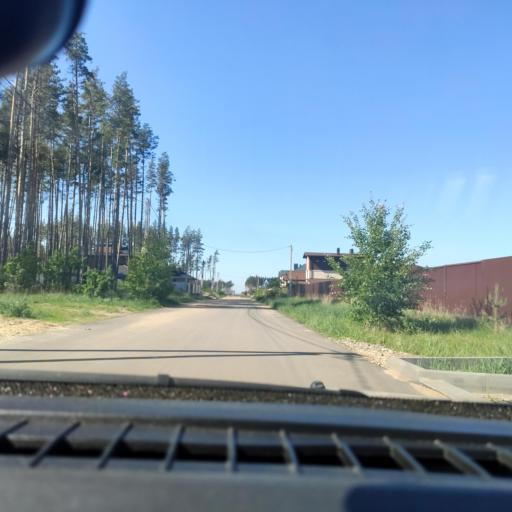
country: RU
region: Voronezj
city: Podgornoye
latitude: 51.7820
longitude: 39.1479
